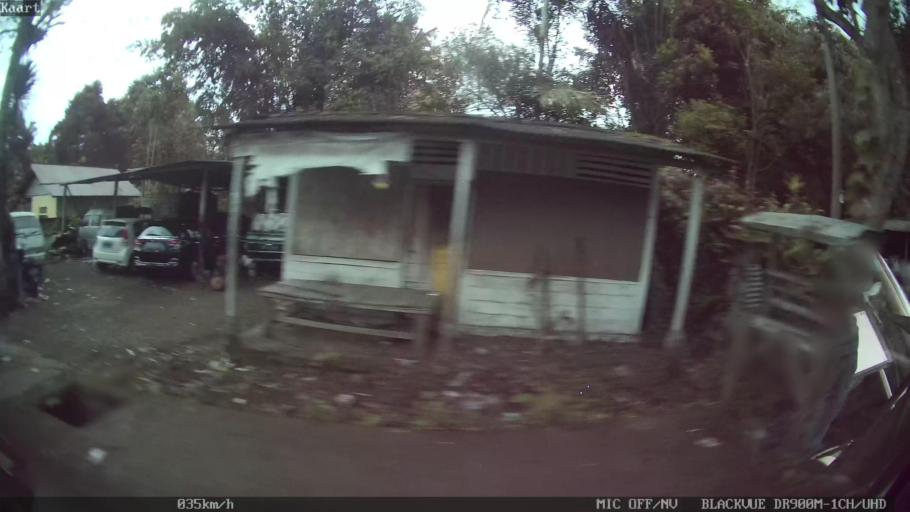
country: ID
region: Bali
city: Banjar Bias
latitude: -8.3751
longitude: 115.4187
